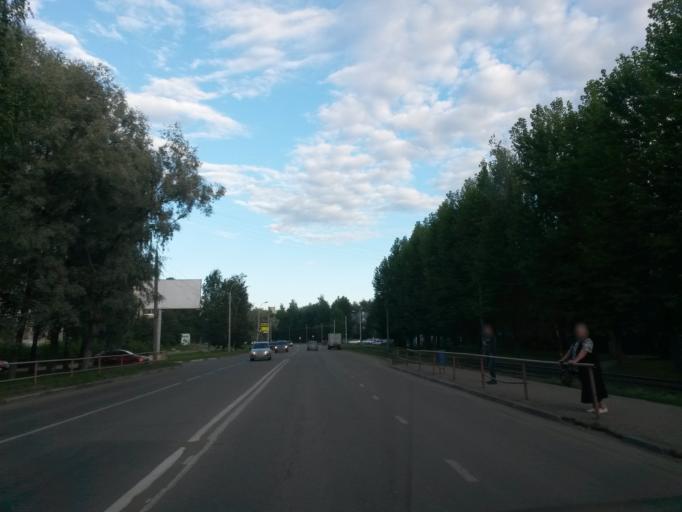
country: RU
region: Jaroslavl
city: Yaroslavl
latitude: 57.6839
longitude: 39.7698
